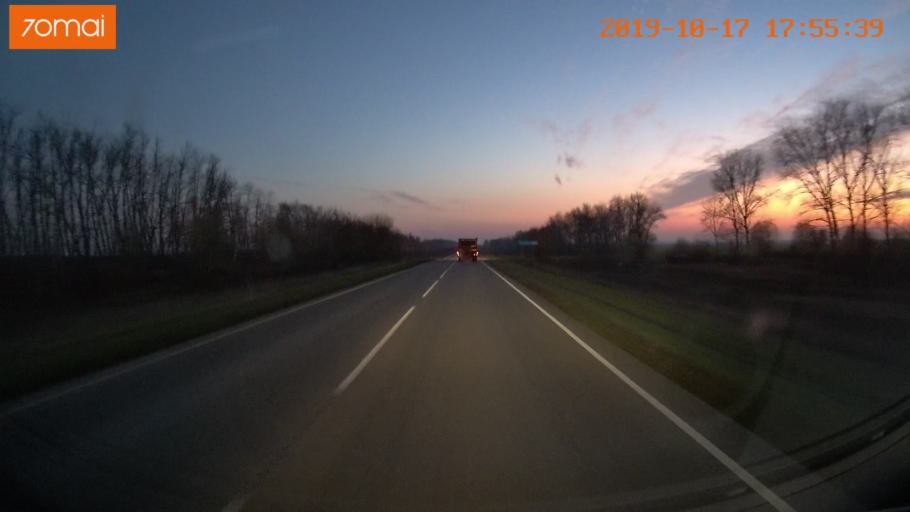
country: RU
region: Tula
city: Kurkino
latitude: 53.5912
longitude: 38.6557
